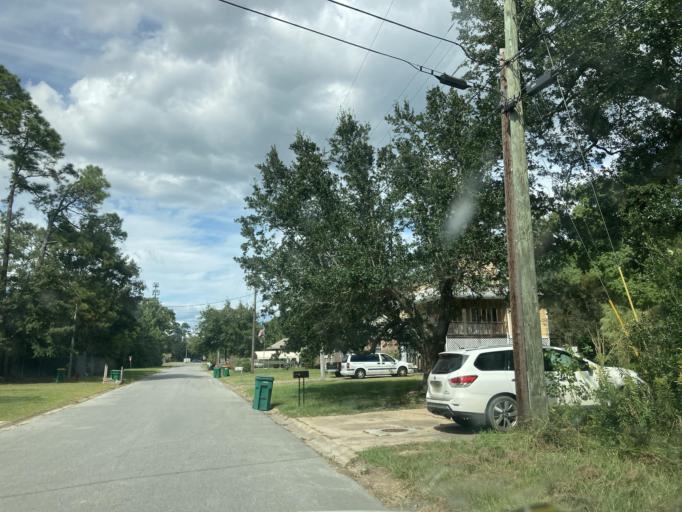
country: US
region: Mississippi
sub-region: Jackson County
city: Saint Martin
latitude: 30.4383
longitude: -88.8760
